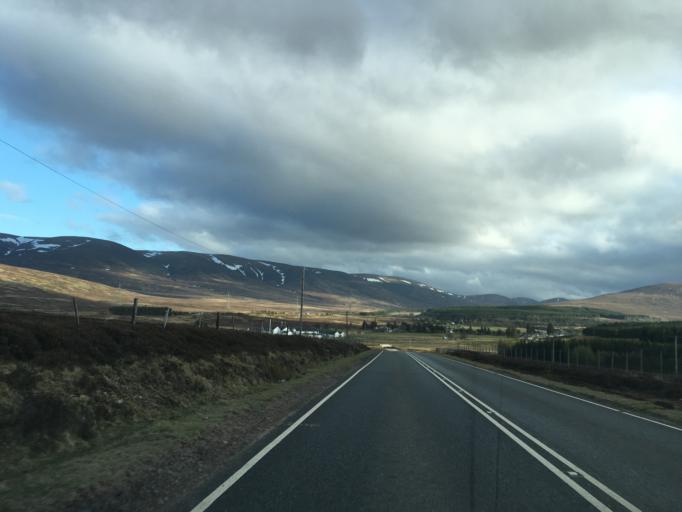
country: GB
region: Scotland
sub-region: Highland
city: Kingussie
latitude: 56.9469
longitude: -4.2435
